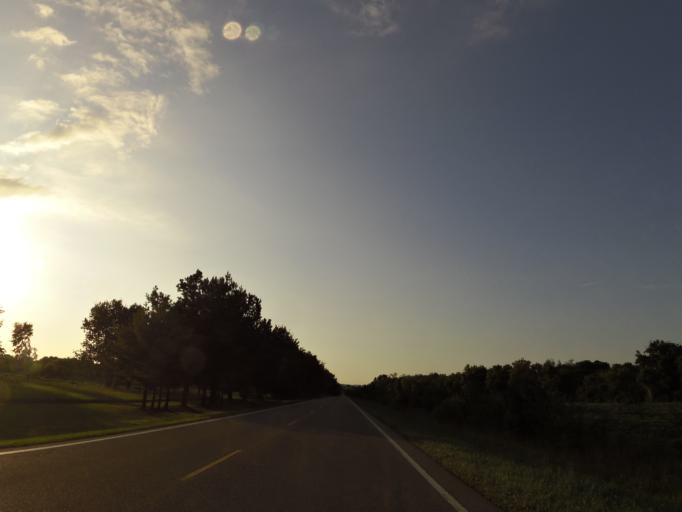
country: US
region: Tennessee
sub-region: Cocke County
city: Newport
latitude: 35.9868
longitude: -83.2840
